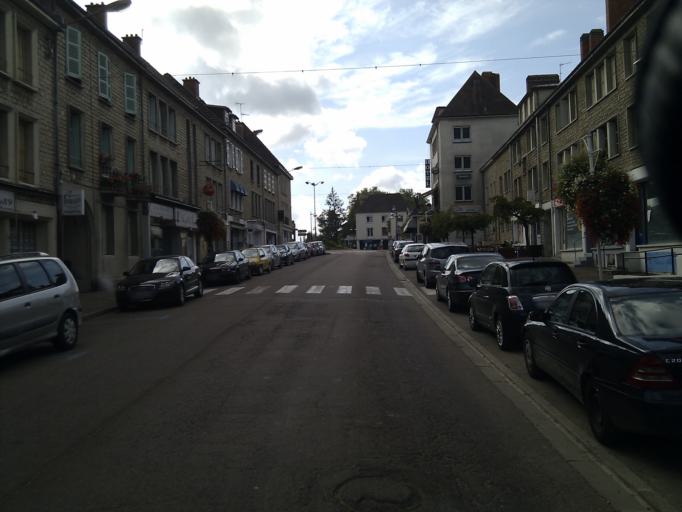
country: FR
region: Bourgogne
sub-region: Departement de la Cote-d'Or
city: Chatillon-sur-Seine
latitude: 47.8580
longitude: 4.5721
